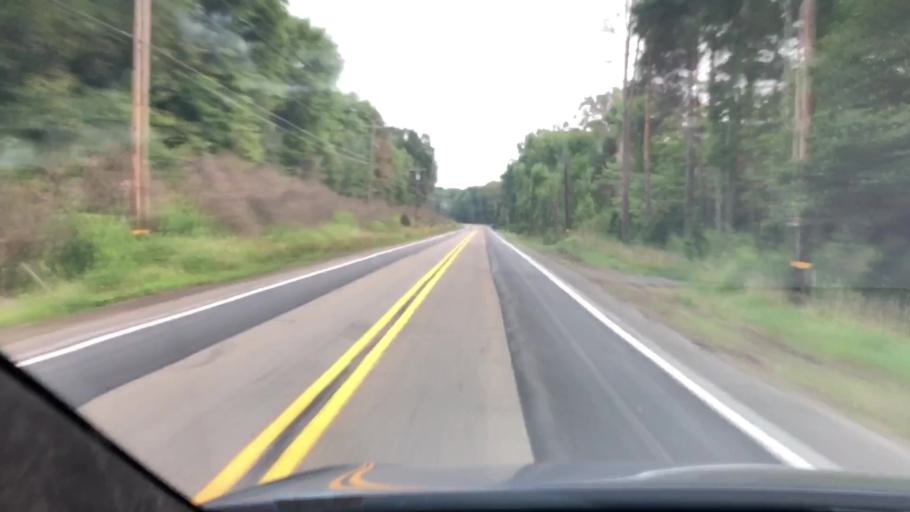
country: US
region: Pennsylvania
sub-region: Butler County
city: Slippery Rock
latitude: 41.0327
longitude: -80.0082
